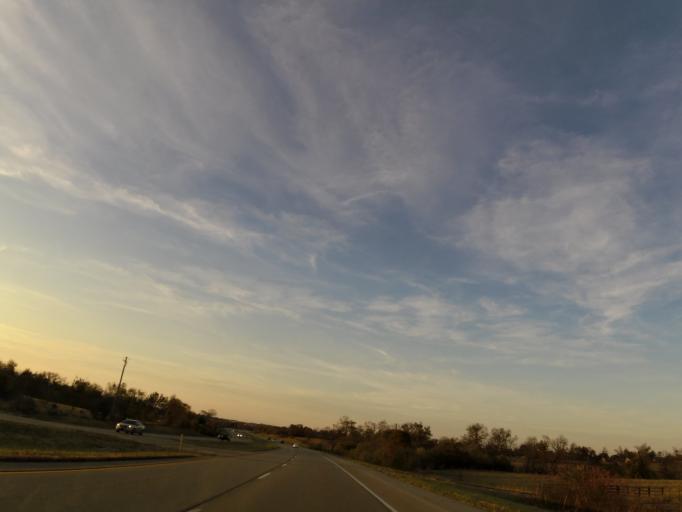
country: US
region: Kentucky
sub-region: Jessamine County
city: Nicholasville
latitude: 37.8563
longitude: -84.5885
